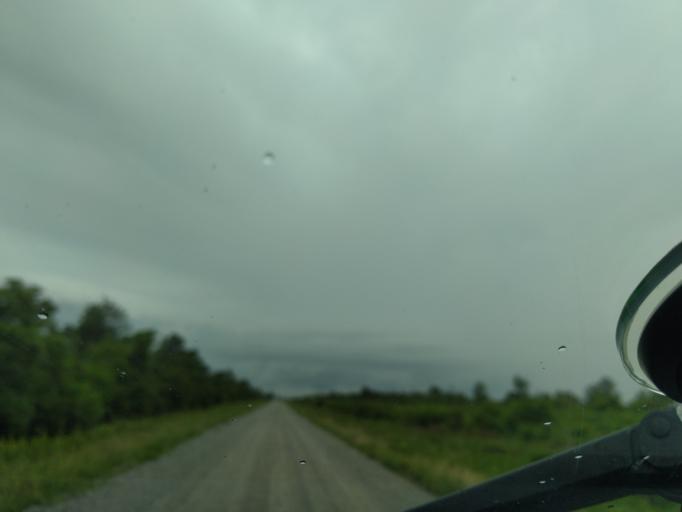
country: US
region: North Carolina
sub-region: Beaufort County
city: Belhaven
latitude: 35.7318
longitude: -76.4429
